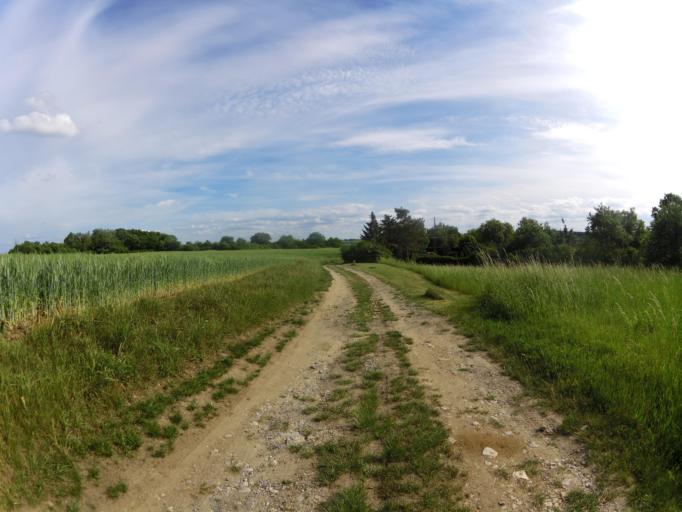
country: DE
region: Bavaria
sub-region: Regierungsbezirk Unterfranken
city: Ochsenfurt
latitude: 49.6734
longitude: 10.0668
